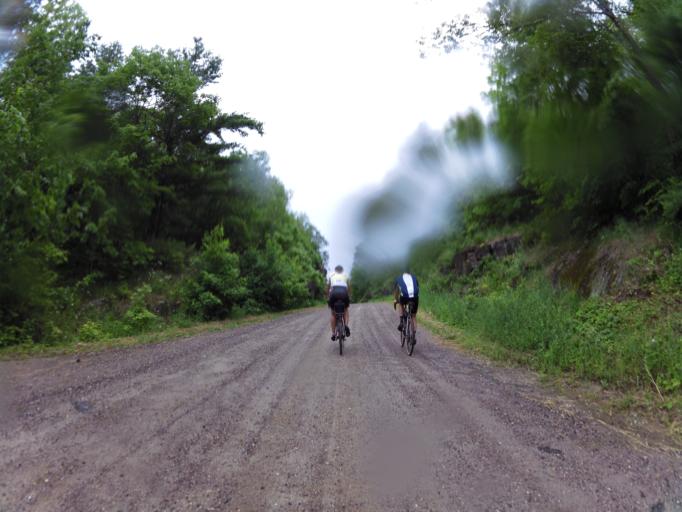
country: CA
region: Ontario
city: Renfrew
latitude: 45.1038
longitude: -76.6060
